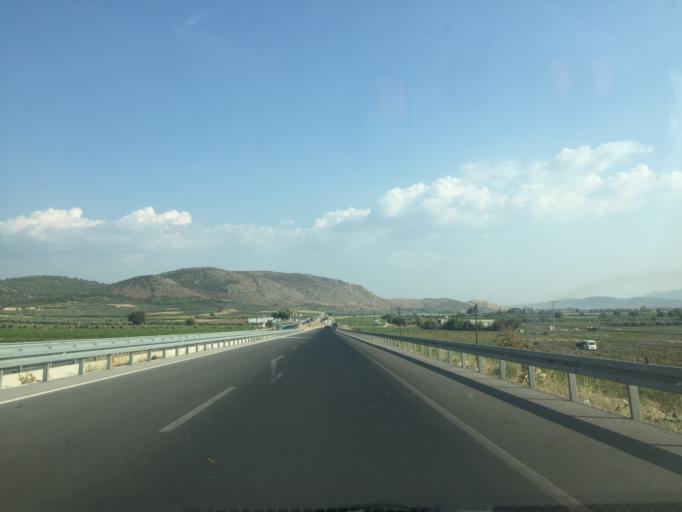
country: TR
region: Manisa
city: Golmarmara
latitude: 38.7945
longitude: 27.8980
